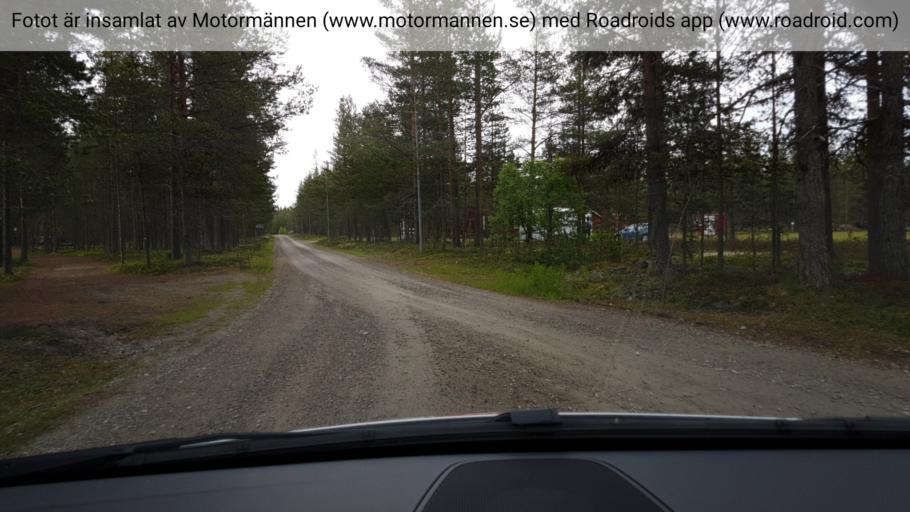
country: SE
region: Jaemtland
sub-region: Harjedalens Kommun
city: Sveg
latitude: 62.2406
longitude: 13.3370
